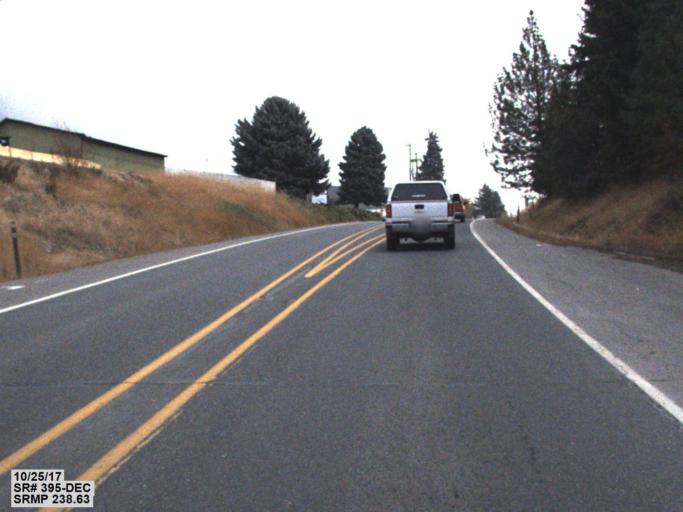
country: US
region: Washington
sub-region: Stevens County
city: Kettle Falls
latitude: 48.6099
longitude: -118.0651
